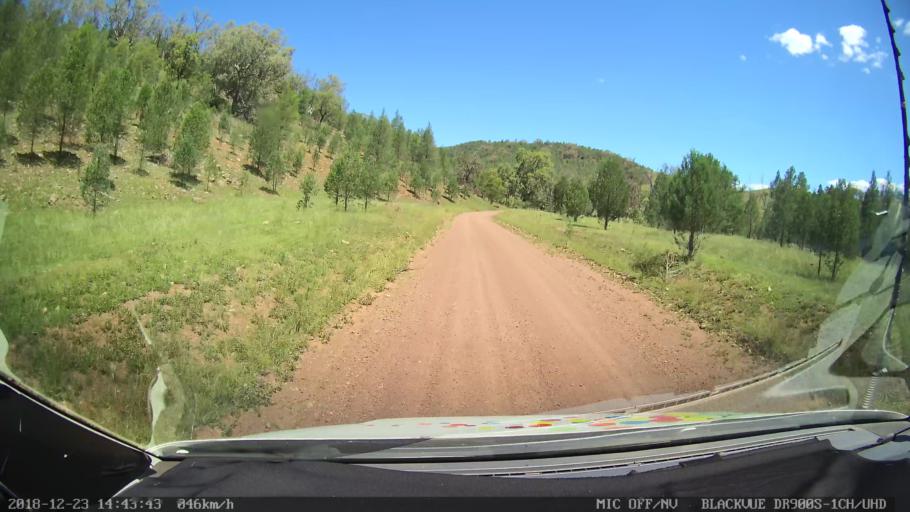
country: AU
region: New South Wales
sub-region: Tamworth Municipality
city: Manilla
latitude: -30.6429
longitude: 150.8977
